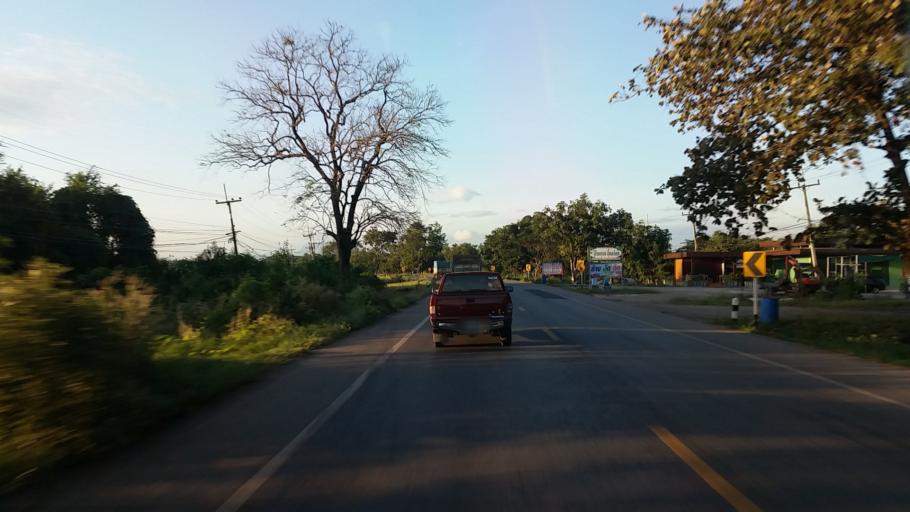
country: TH
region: Lop Buri
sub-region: Amphoe Lam Sonthi
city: Lam Sonthi
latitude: 15.2926
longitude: 101.3521
